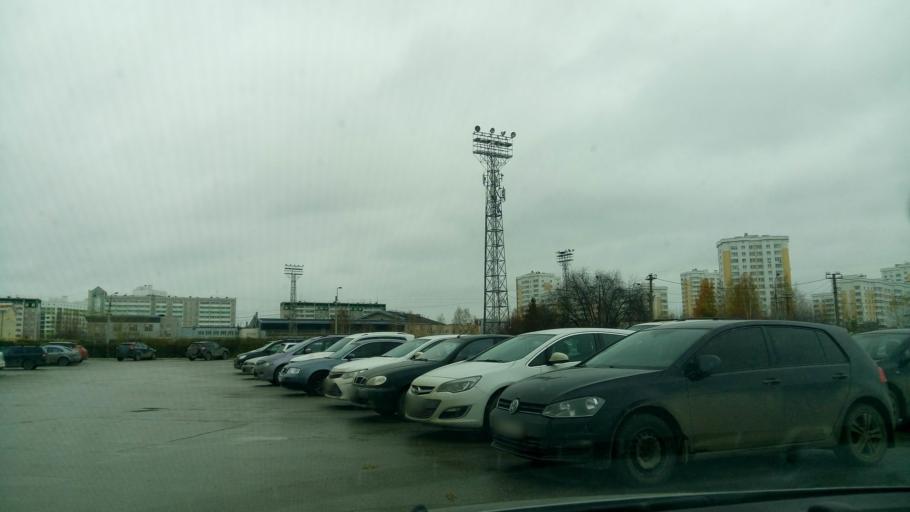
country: RU
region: Sverdlovsk
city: Verkhnyaya Pyshma
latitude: 56.9694
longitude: 60.5784
